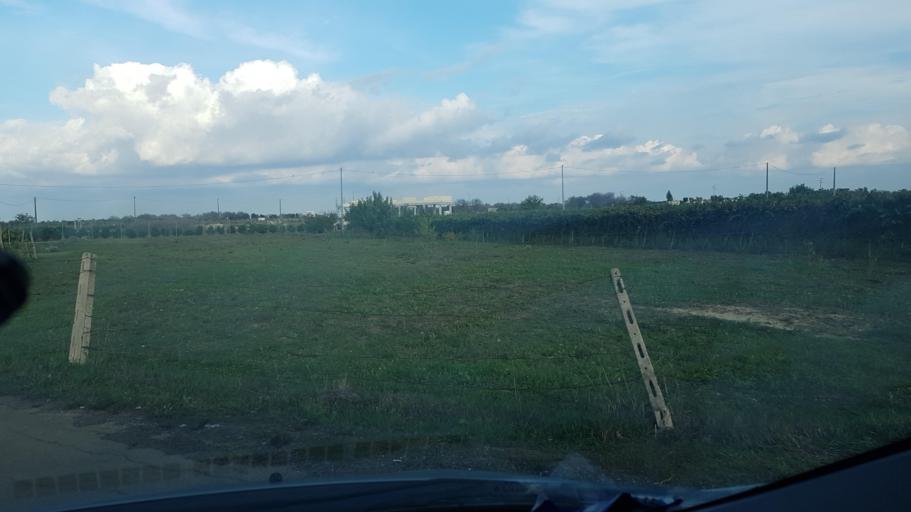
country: IT
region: Apulia
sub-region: Provincia di Lecce
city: Veglie
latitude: 40.3301
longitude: 17.9787
